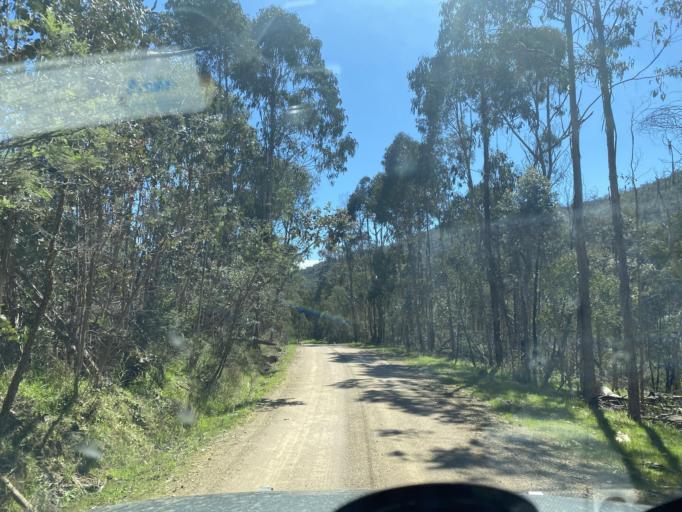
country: AU
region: Victoria
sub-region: Benalla
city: Benalla
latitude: -36.7027
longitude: 146.1786
